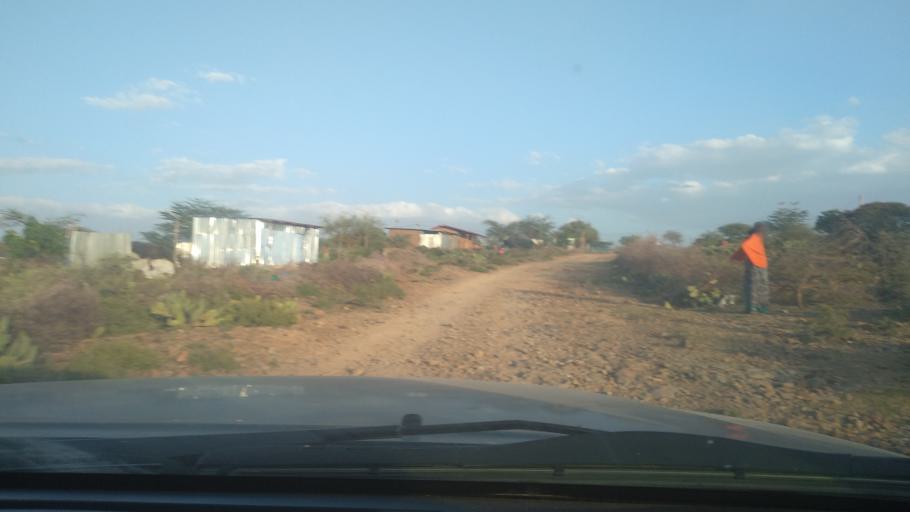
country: ET
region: Oromiya
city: Asbe Teferi
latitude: 9.2721
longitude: 40.8079
